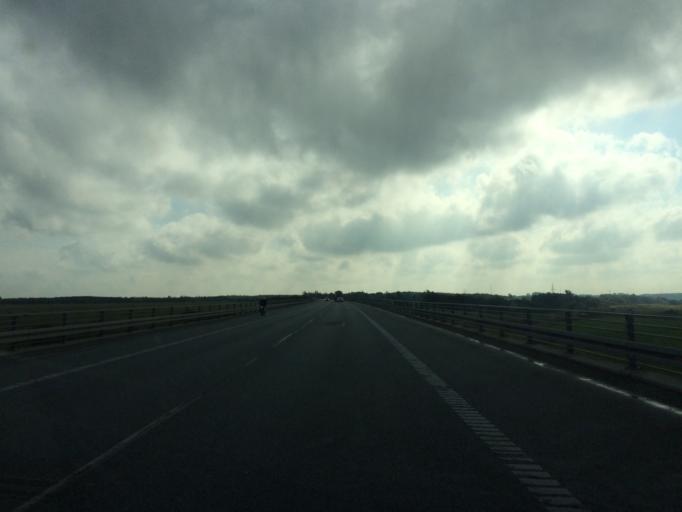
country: DK
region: Central Jutland
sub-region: Skive Kommune
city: Skive
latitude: 56.5461
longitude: 8.9950
